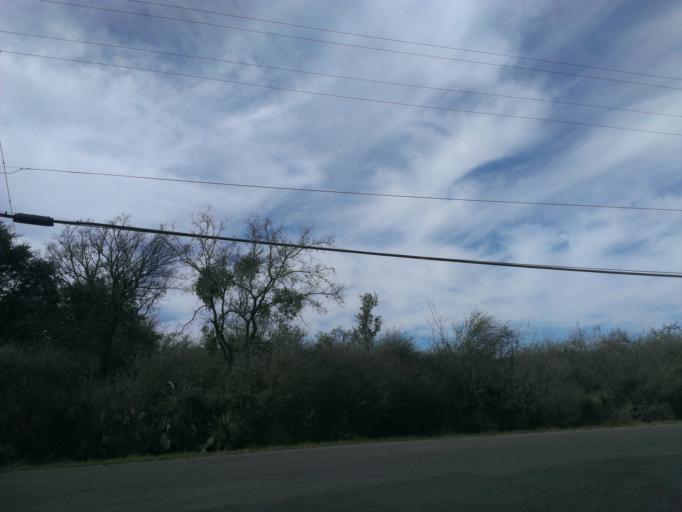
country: US
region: Texas
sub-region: Burnet County
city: Granite Shoals
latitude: 30.5744
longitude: -98.3898
